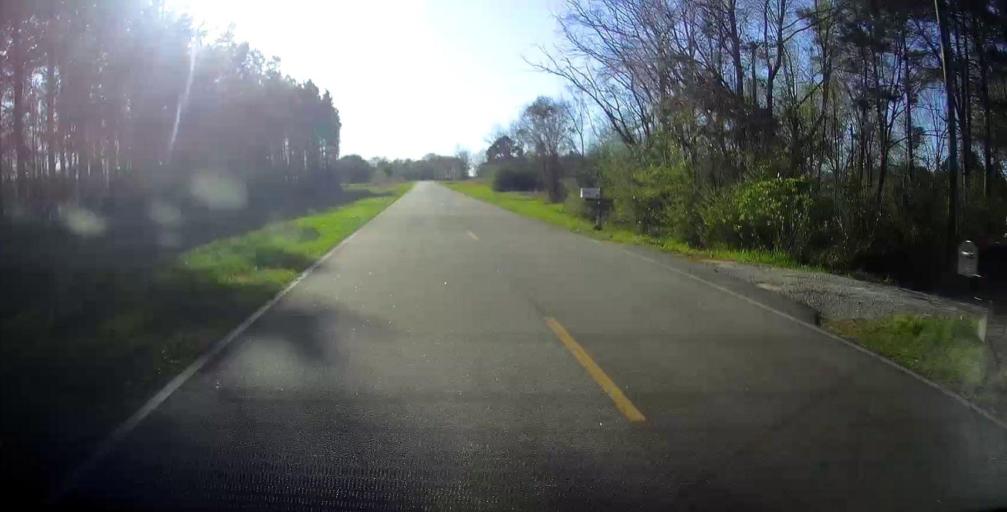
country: US
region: Georgia
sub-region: Pulaski County
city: Hawkinsville
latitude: 32.3479
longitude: -83.6107
